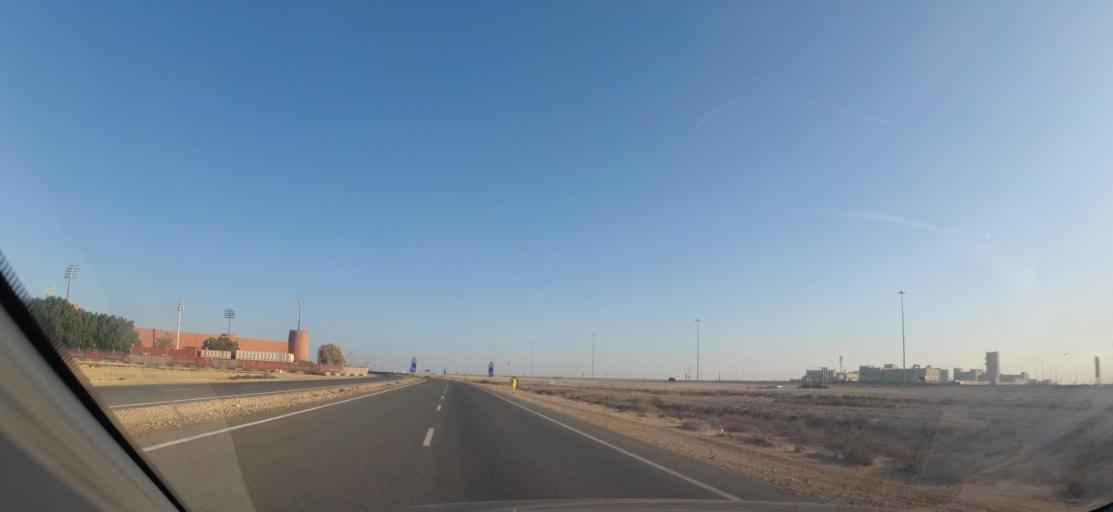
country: QA
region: Madinat ash Shamal
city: Ar Ru'ays
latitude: 26.1190
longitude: 51.2173
